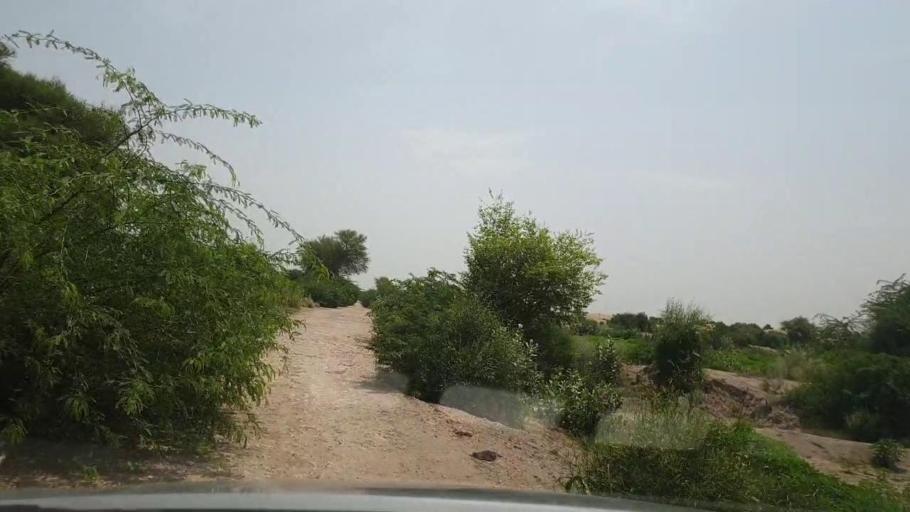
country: PK
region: Sindh
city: Pano Aqil
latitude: 27.5787
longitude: 69.1773
